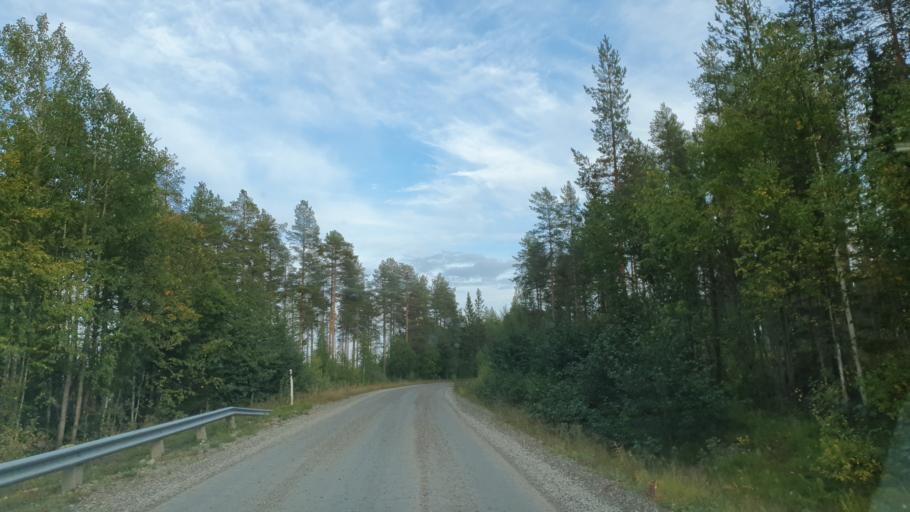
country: FI
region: Kainuu
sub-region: Kehys-Kainuu
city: Kuhmo
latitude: 64.4075
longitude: 29.5466
